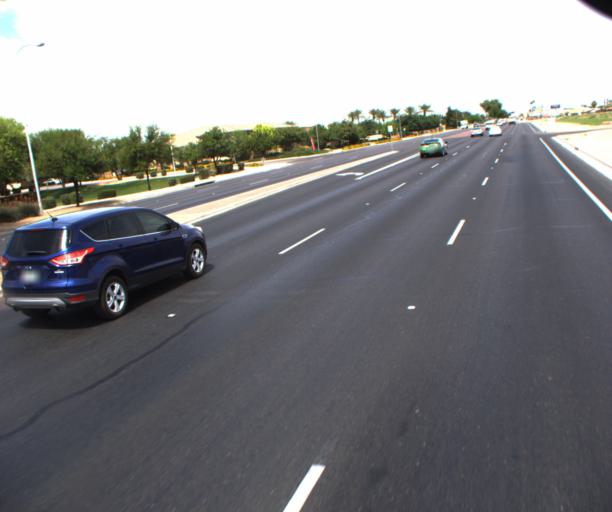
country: US
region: Arizona
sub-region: Maricopa County
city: Chandler
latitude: 33.2687
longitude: -111.8413
